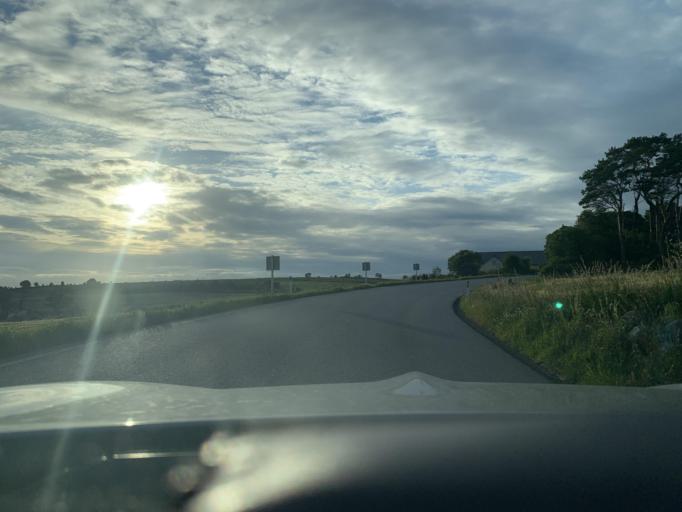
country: NO
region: Rogaland
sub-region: Time
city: Bryne
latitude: 58.7080
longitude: 5.6915
